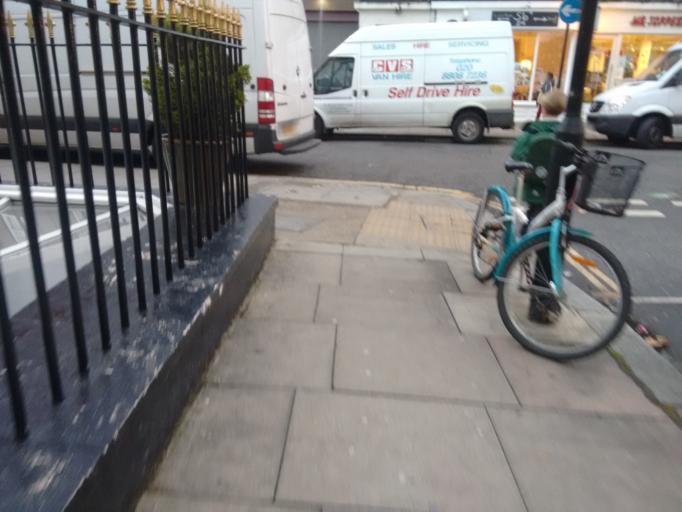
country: GB
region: England
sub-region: Greater London
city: London
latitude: 51.5173
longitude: -0.1297
